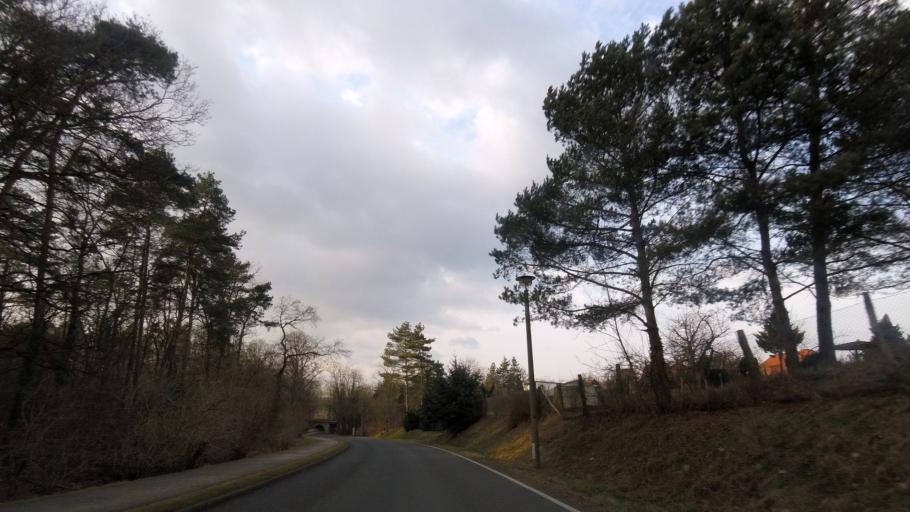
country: DE
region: Brandenburg
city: Belzig
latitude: 52.1346
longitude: 12.5855
